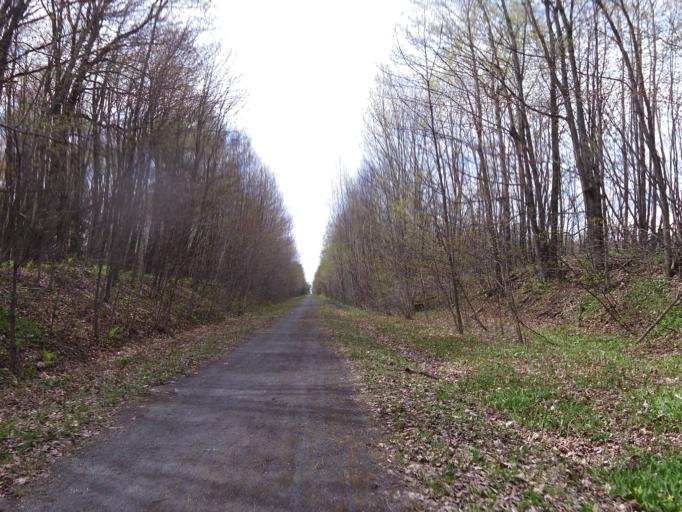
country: CA
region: Ontario
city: Hawkesbury
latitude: 45.5335
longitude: -74.6929
